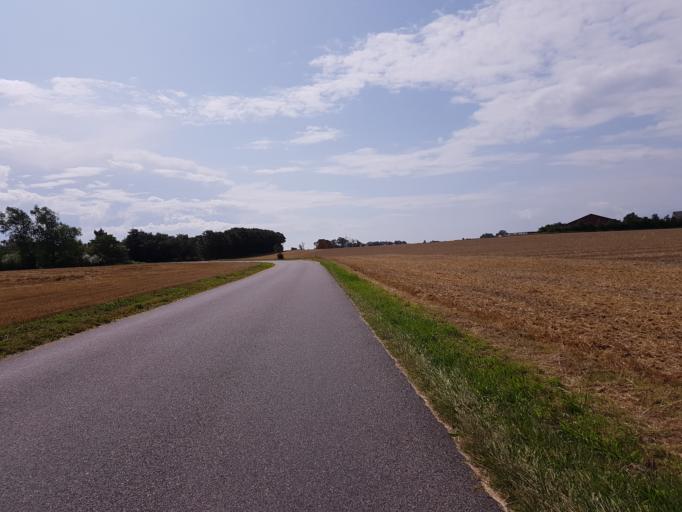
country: DK
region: Zealand
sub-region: Guldborgsund Kommune
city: Nykobing Falster
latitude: 54.5999
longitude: 11.9426
